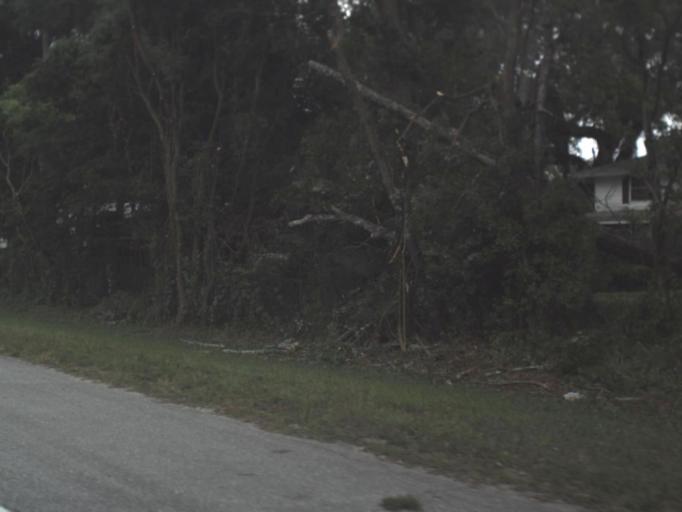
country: US
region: Florida
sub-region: Duval County
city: Jacksonville
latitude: 30.2923
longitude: -81.5895
